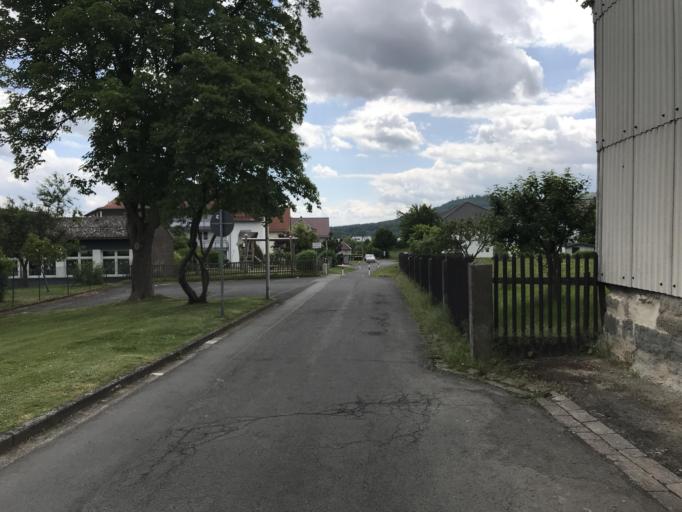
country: DE
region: Hesse
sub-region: Regierungsbezirk Kassel
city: Baunatal
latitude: 51.2721
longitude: 9.3745
